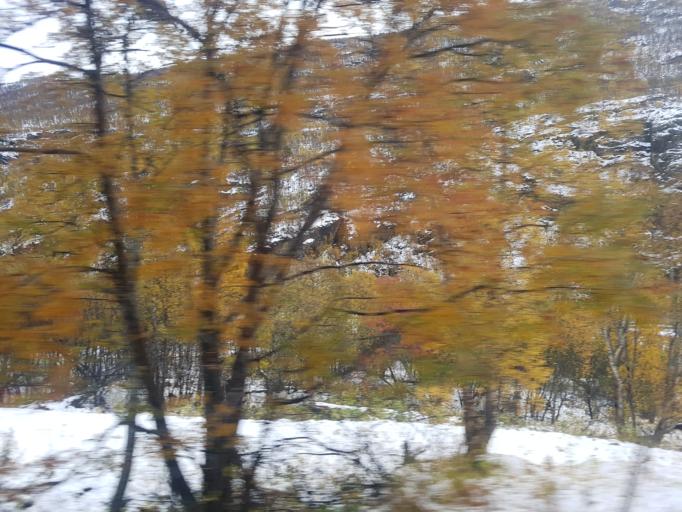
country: NO
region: Sor-Trondelag
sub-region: Oppdal
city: Oppdal
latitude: 62.3940
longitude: 9.6367
